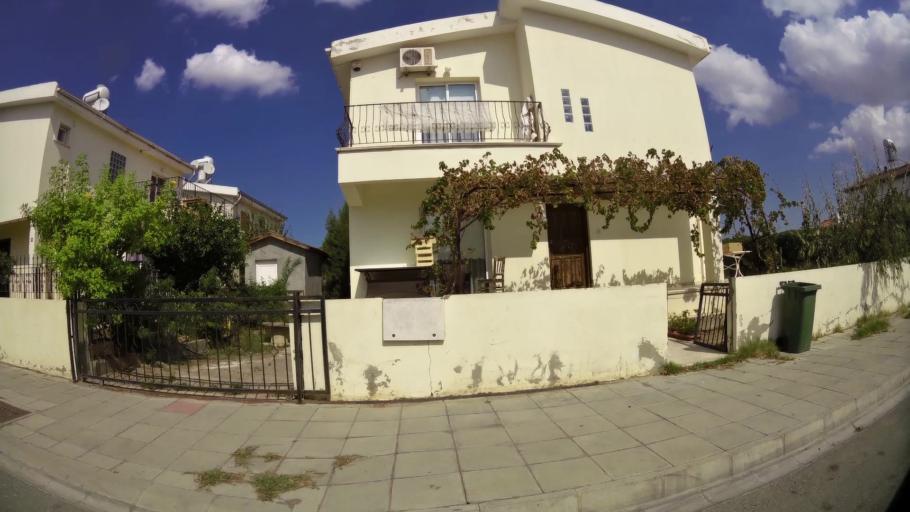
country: CY
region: Lefkosia
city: Nicosia
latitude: 35.2226
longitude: 33.2952
